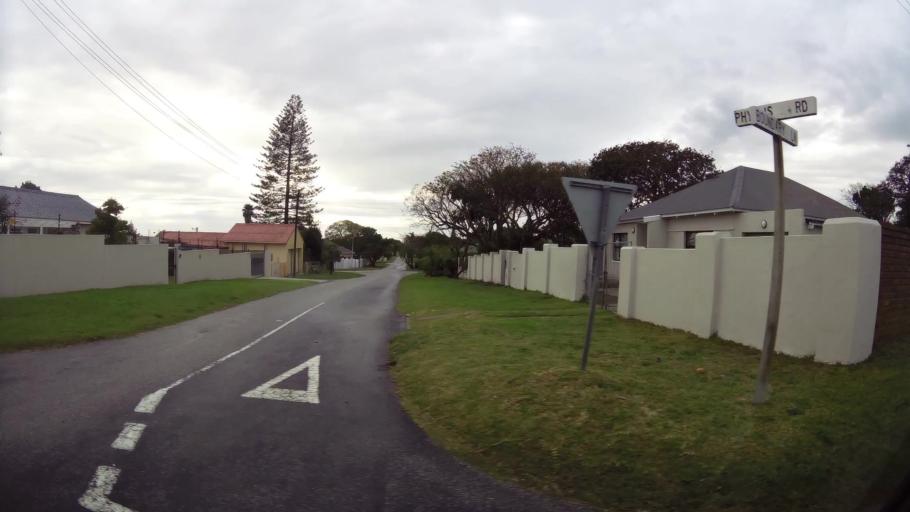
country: ZA
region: Eastern Cape
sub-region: Nelson Mandela Bay Metropolitan Municipality
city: Port Elizabeth
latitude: -33.9970
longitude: 25.5287
